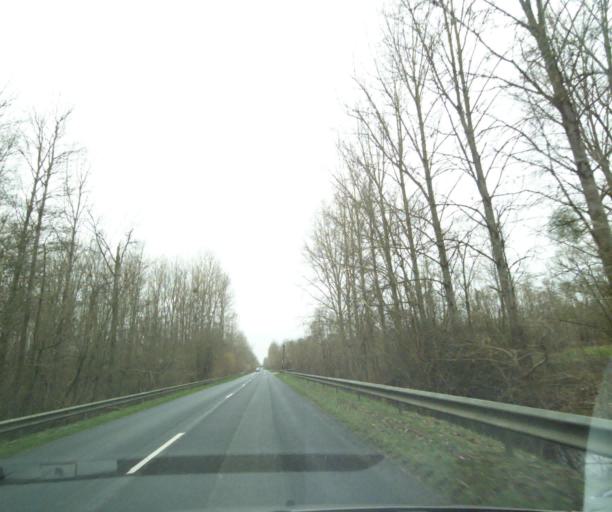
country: FR
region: Picardie
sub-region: Departement de l'Oise
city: Noyon
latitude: 49.5594
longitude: 3.0376
